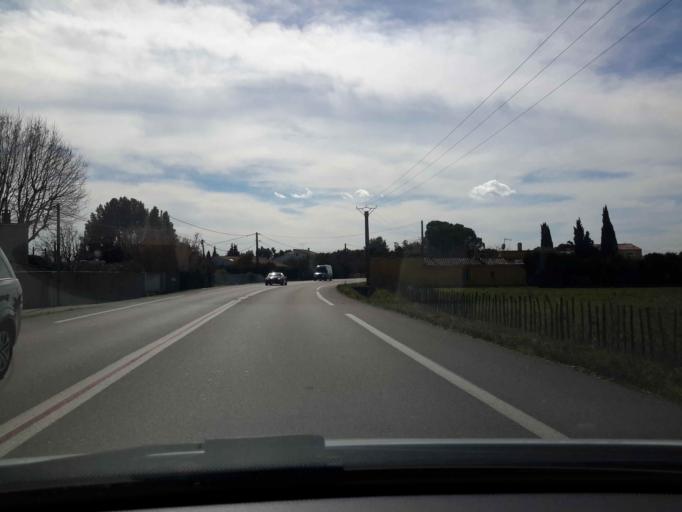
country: FR
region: Languedoc-Roussillon
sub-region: Departement du Gard
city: Vauvert
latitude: 43.7074
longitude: 4.2624
